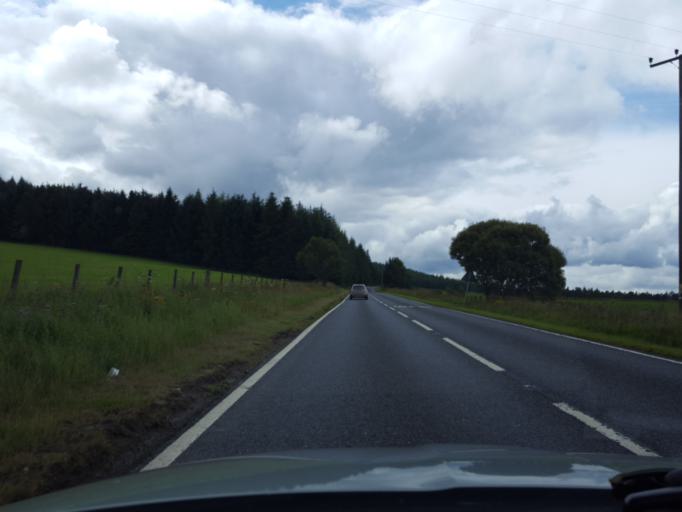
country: GB
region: Scotland
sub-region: Moray
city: Rothes
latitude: 57.4082
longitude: -3.3851
